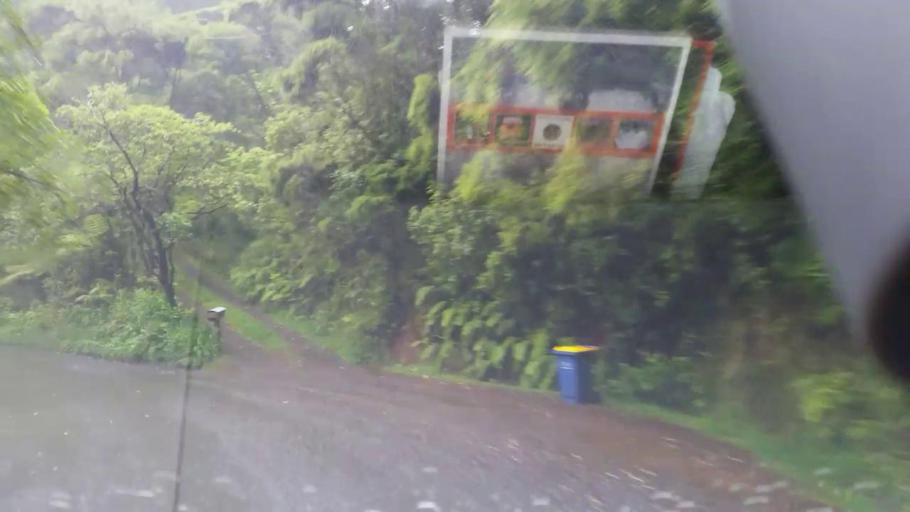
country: NZ
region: Auckland
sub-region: Auckland
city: Waitakere
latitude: -36.9164
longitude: 174.5650
